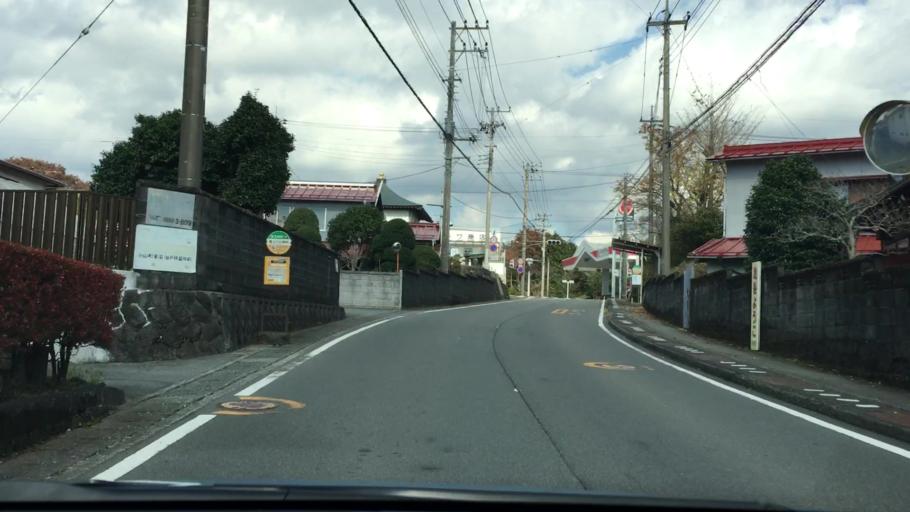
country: JP
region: Shizuoka
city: Gotemba
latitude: 35.3494
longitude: 138.9448
